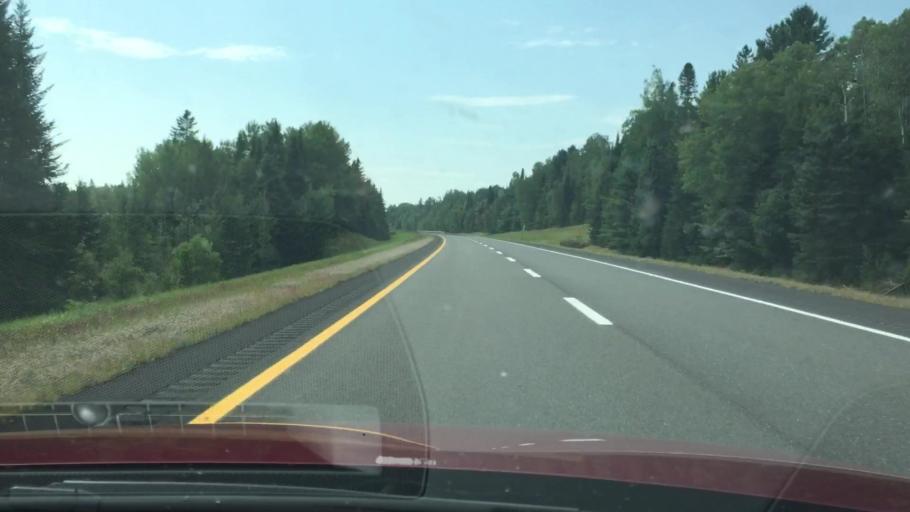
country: US
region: Maine
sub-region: Penobscot County
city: Patten
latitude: 46.0447
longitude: -68.2581
